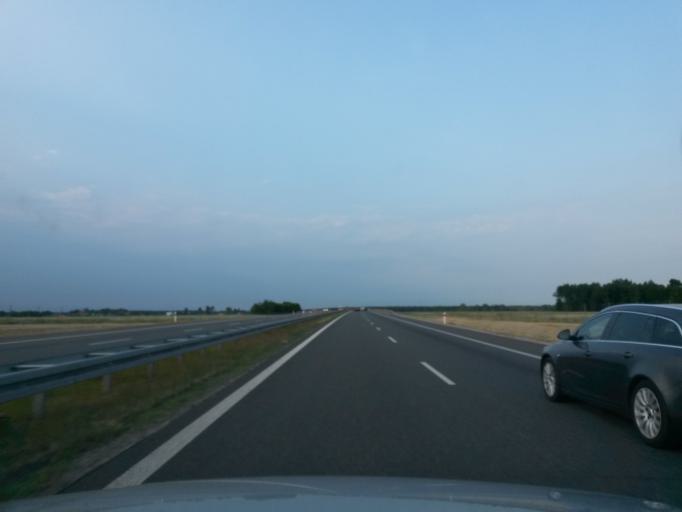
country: PL
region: Lower Silesian Voivodeship
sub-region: Powiat olesnicki
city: Twardogora
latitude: 51.2755
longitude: 17.5600
